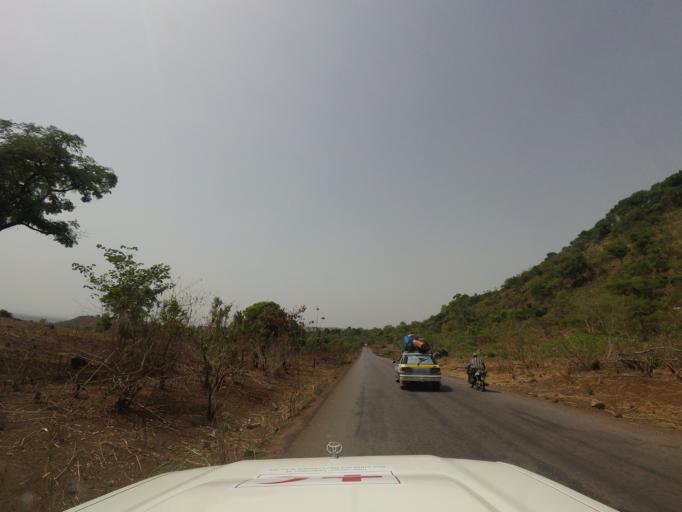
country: GN
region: Mamou
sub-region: Mamou Prefecture
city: Mamou
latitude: 10.2036
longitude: -12.4668
